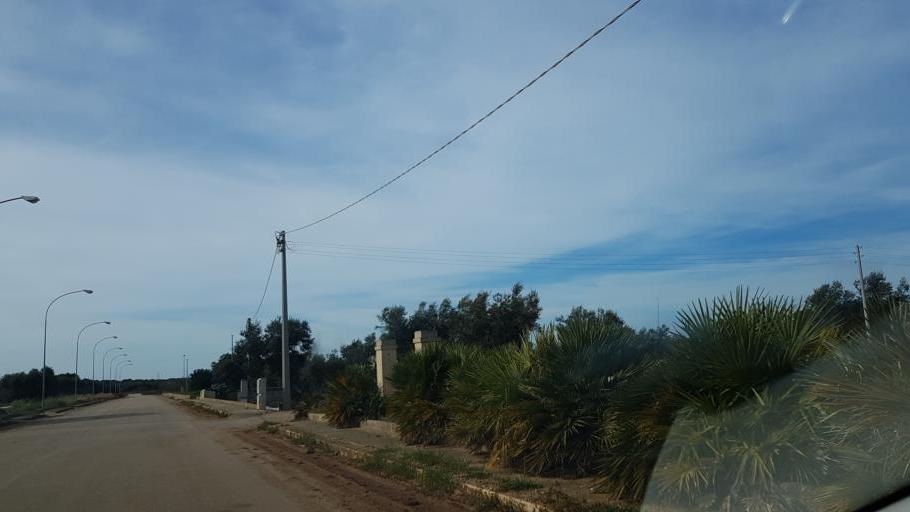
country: IT
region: Apulia
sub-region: Provincia di Brindisi
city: Fasano
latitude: 40.8946
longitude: 17.3615
